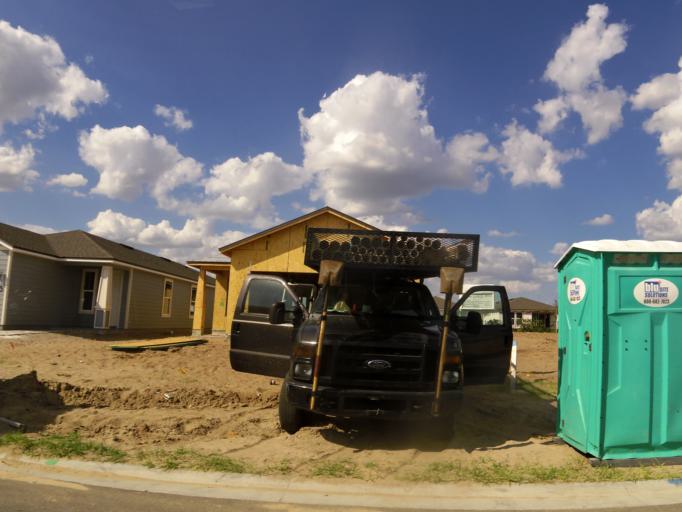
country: US
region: Florida
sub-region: Saint Johns County
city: Palm Valley
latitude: 30.1721
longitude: -81.5092
